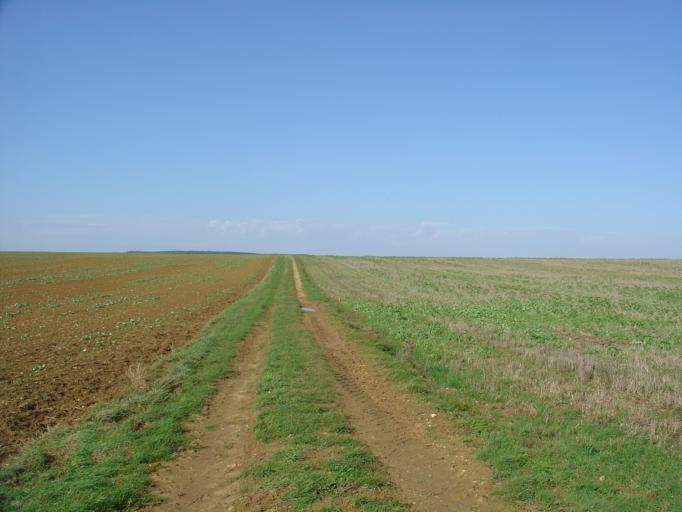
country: FR
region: Lorraine
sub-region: Departement de Meurthe-et-Moselle
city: Colombey-les-Belles
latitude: 48.5582
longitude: 5.9072
